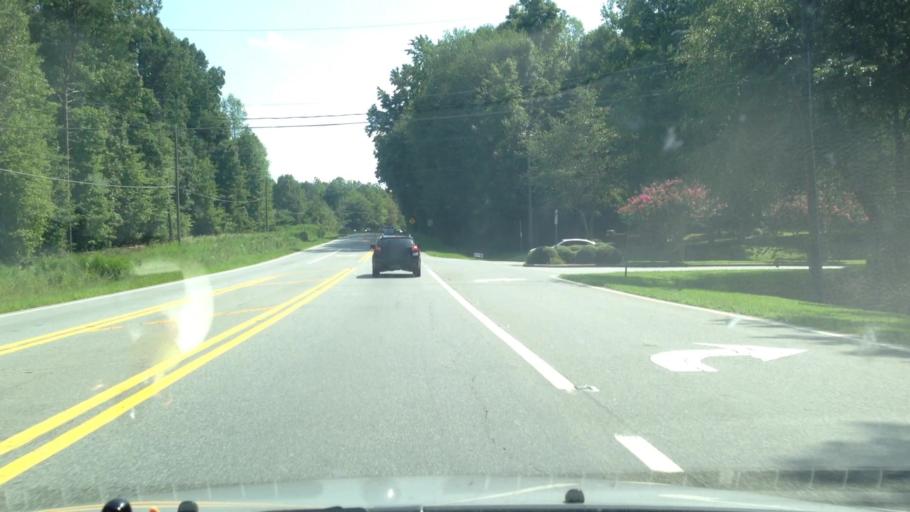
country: US
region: North Carolina
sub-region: Guilford County
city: Oak Ridge
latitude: 36.1875
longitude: -79.9861
